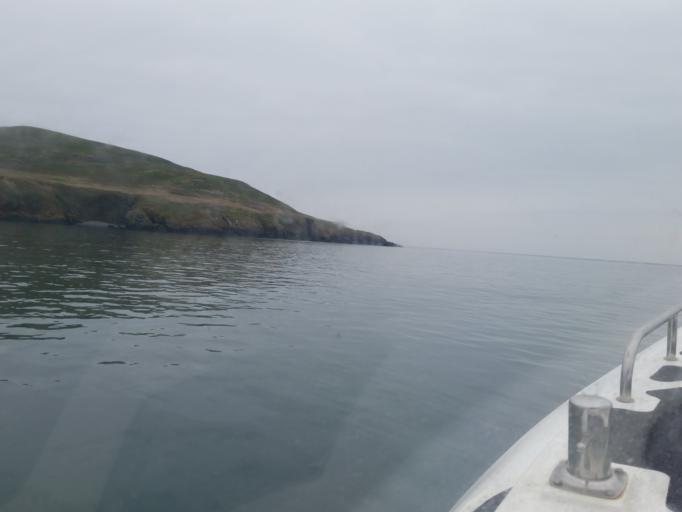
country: IE
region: Leinster
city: Portraine
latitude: 53.4811
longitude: -6.0221
